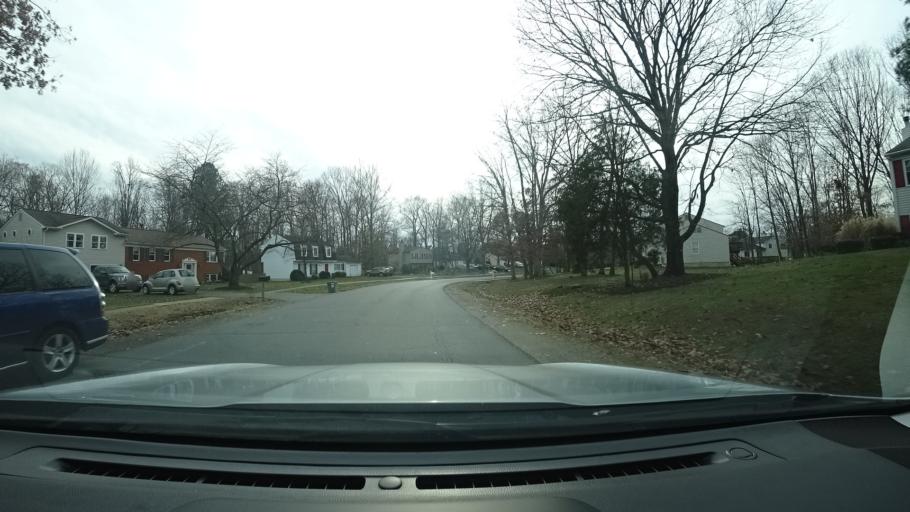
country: US
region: Virginia
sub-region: Fairfax County
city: Oak Hill
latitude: 38.9398
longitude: -77.3811
